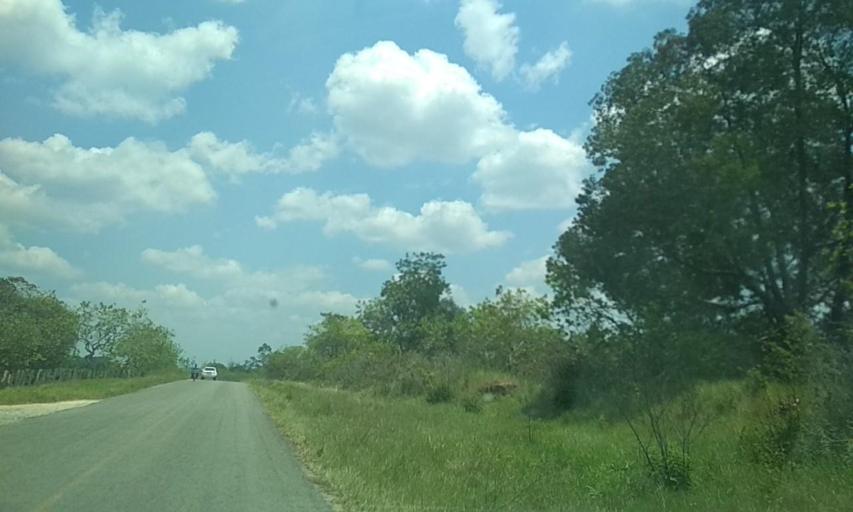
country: MX
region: Tabasco
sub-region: Huimanguillo
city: Francisco Rueda
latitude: 17.7869
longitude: -93.8316
